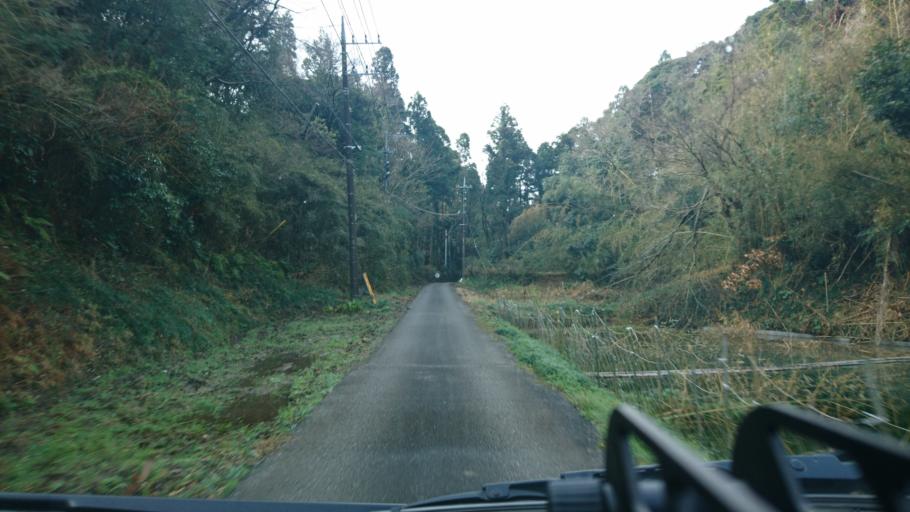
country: JP
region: Chiba
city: Kisarazu
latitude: 35.3215
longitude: 139.9687
